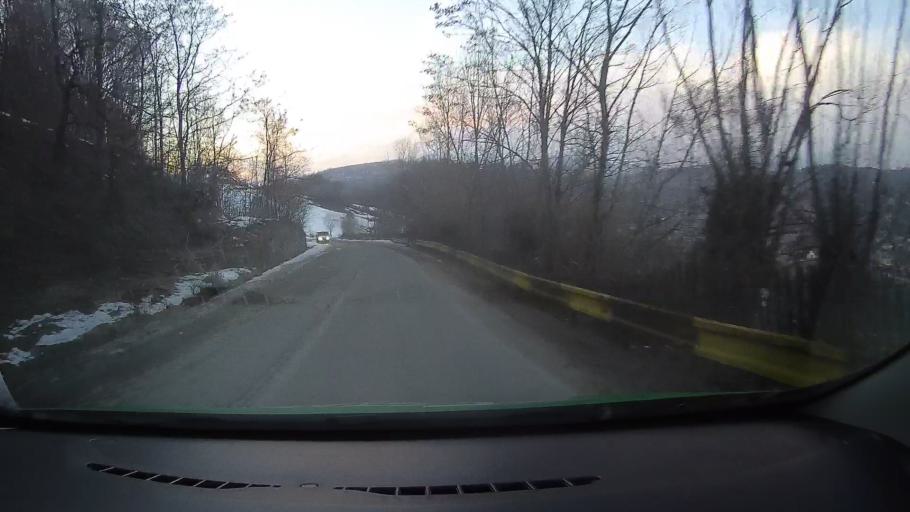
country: RO
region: Prahova
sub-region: Comuna Secaria
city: Secaria
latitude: 45.2707
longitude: 25.6833
